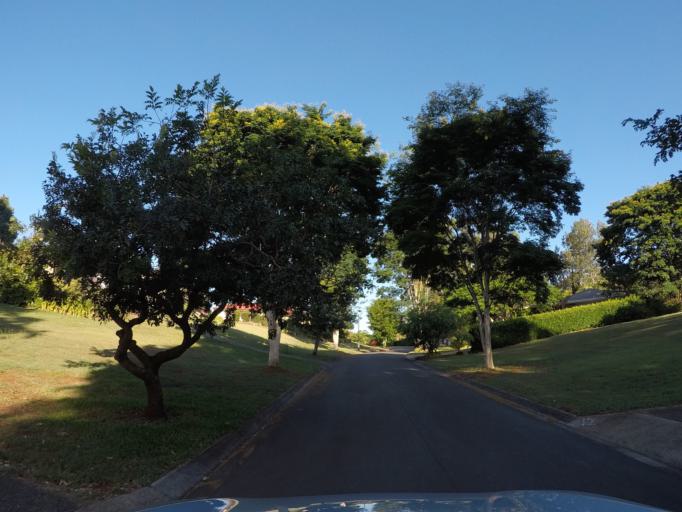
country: AU
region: Queensland
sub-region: Sunshine Coast
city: Nambour
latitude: -26.6298
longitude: 152.8662
